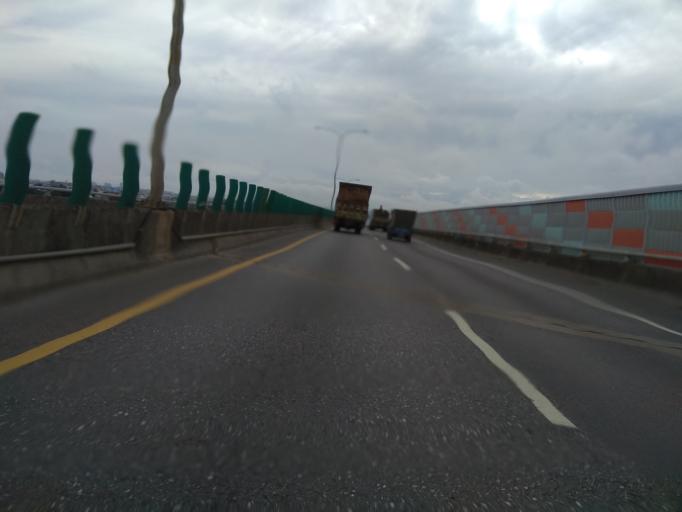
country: TW
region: Taiwan
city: Daxi
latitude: 24.9309
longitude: 121.2006
